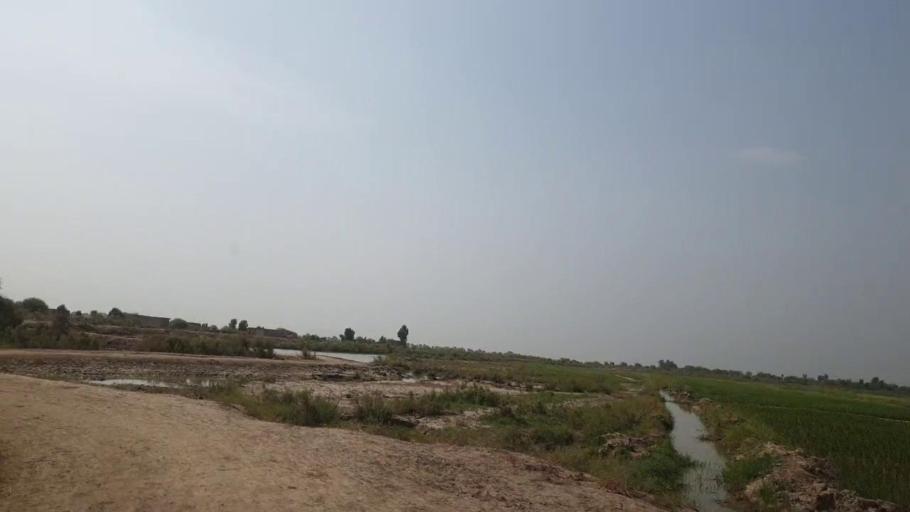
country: PK
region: Sindh
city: Dokri
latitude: 27.4121
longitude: 68.2017
